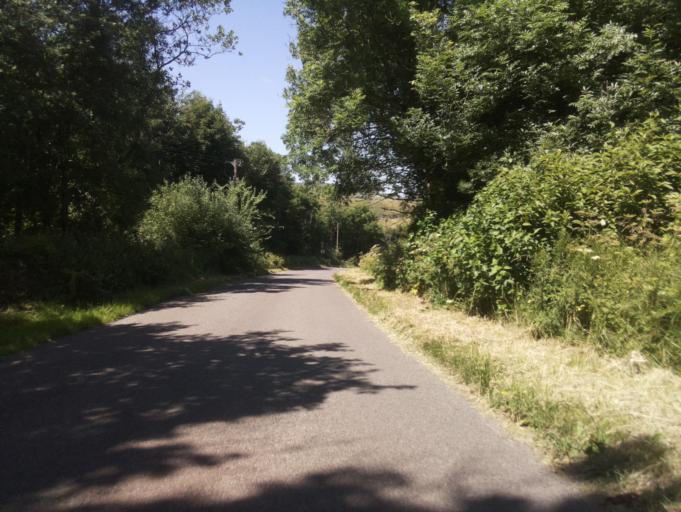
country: GB
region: England
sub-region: Derbyshire
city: Buxton
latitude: 53.2869
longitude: -1.8611
